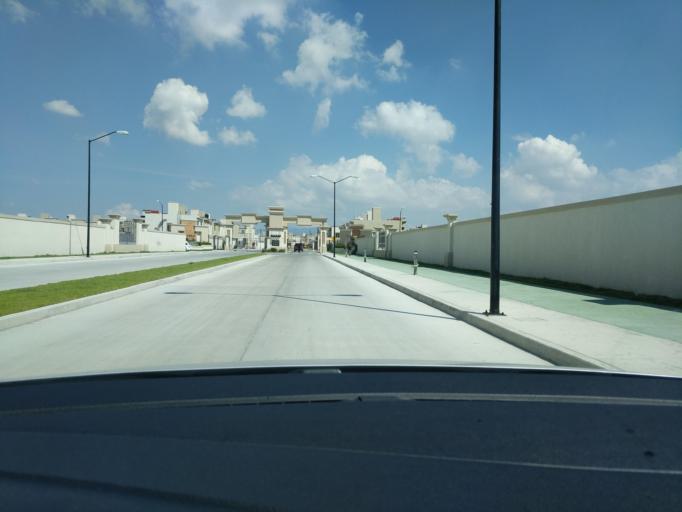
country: MX
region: Hidalgo
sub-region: Zempoala
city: Lindavista
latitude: 20.0111
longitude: -98.7802
